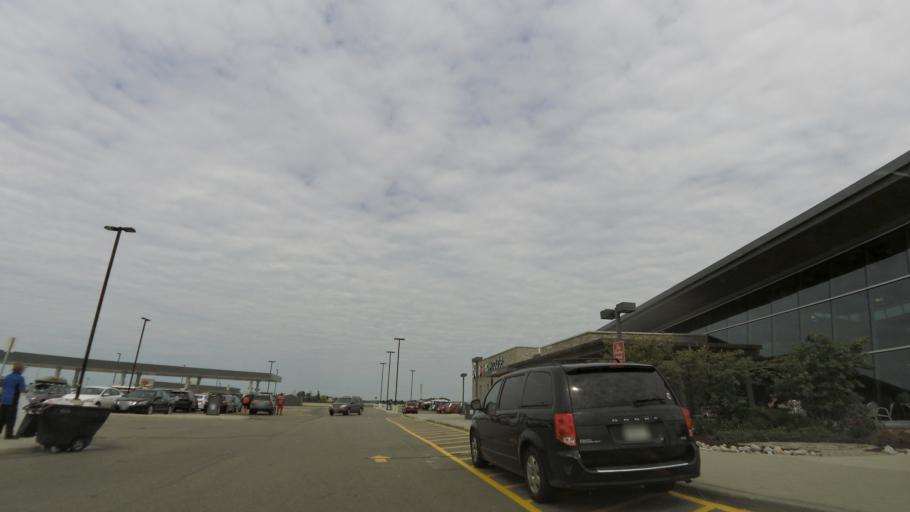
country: CA
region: Ontario
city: Vaughan
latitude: 43.8948
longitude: -79.5578
